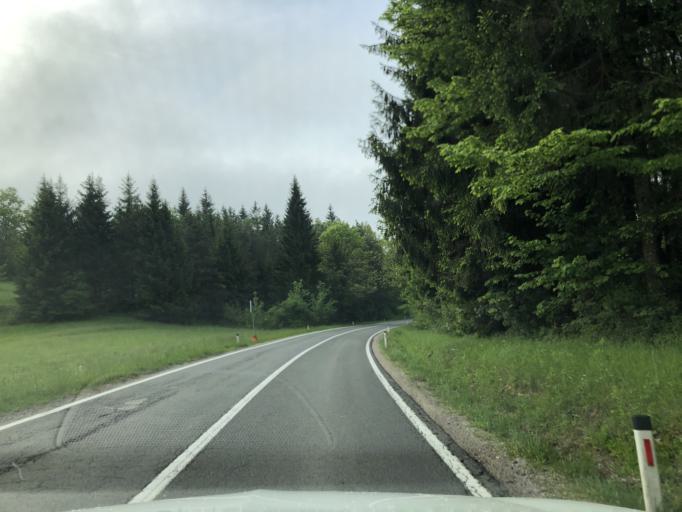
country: SI
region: Velike Lasce
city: Velike Lasce
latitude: 45.8694
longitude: 14.6178
